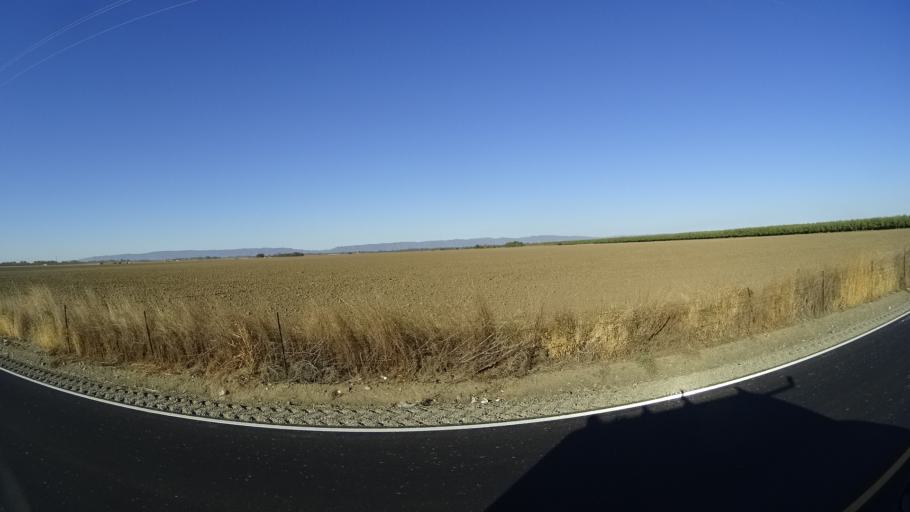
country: US
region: California
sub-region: Yolo County
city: Davis
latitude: 38.5737
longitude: -121.7860
